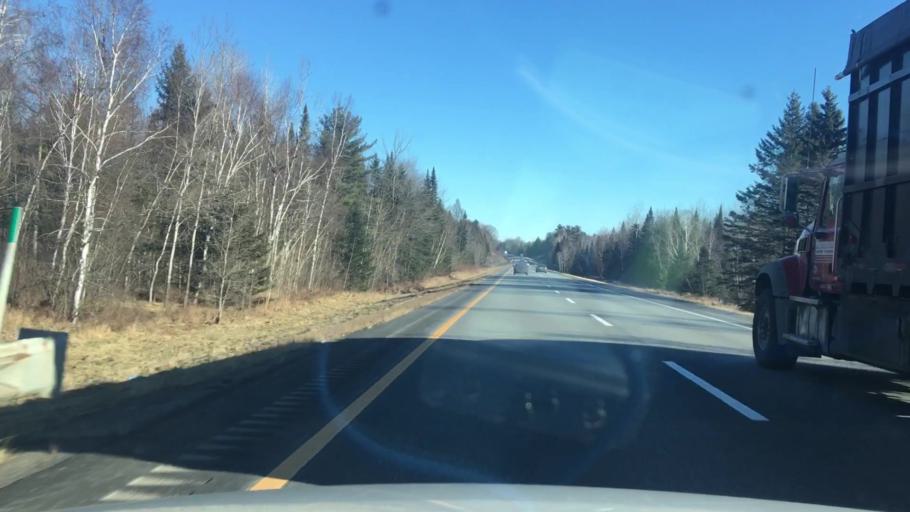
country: US
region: Maine
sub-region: Somerset County
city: Palmyra
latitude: 44.8112
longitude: -69.3512
